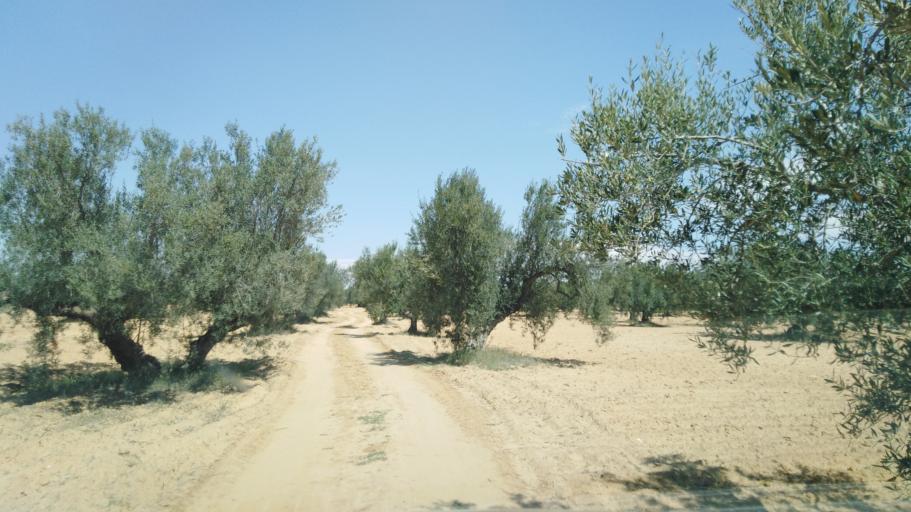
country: TN
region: Safaqis
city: Sfax
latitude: 34.7831
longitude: 10.5277
